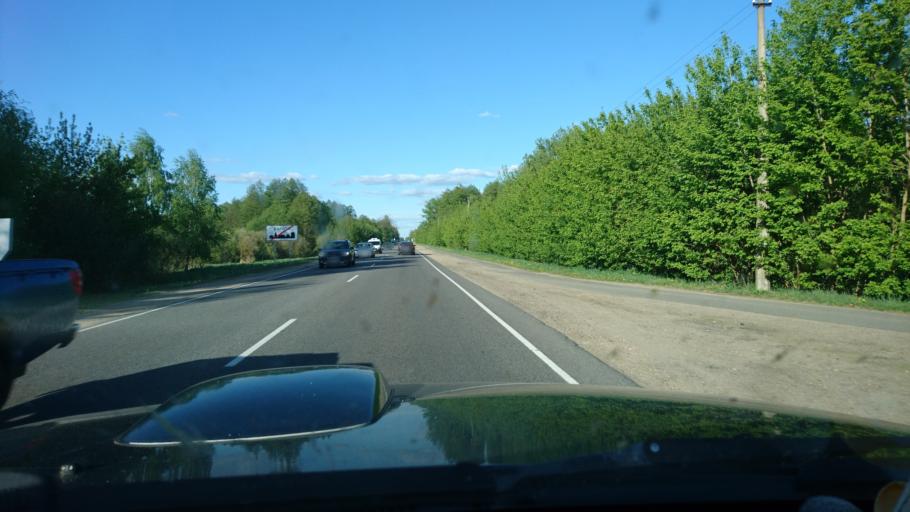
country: BY
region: Brest
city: Byaroza
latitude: 52.5432
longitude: 25.0025
